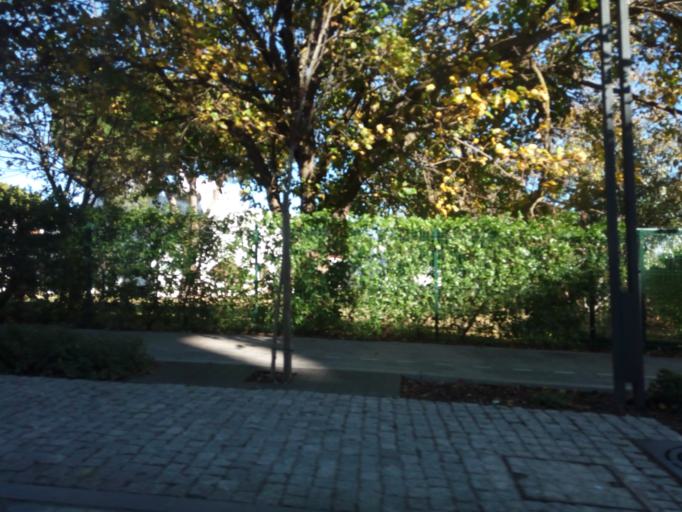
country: PT
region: Faro
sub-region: Loule
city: Vilamoura
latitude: 37.0768
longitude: -8.1148
